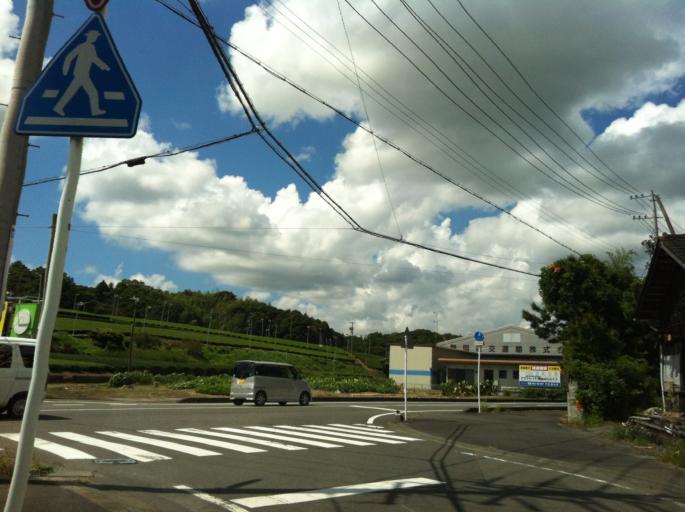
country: JP
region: Shizuoka
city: Kakegawa
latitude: 34.7425
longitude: 138.0754
